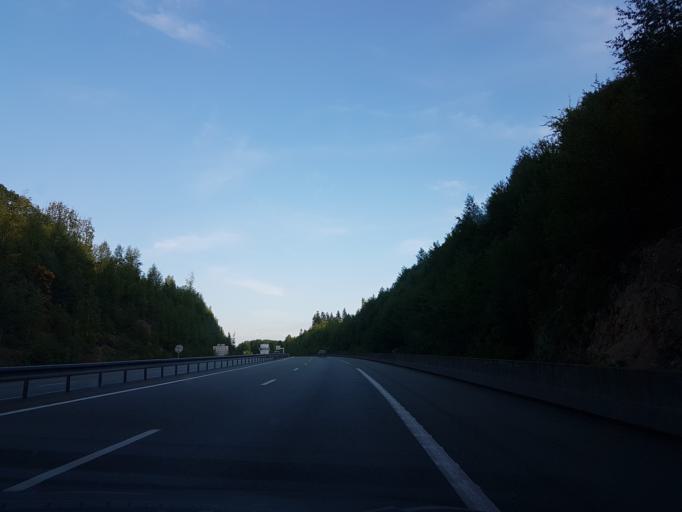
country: FR
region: Franche-Comte
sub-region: Departement de la Haute-Saone
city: Fougerolles
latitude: 47.8538
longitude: 6.3831
